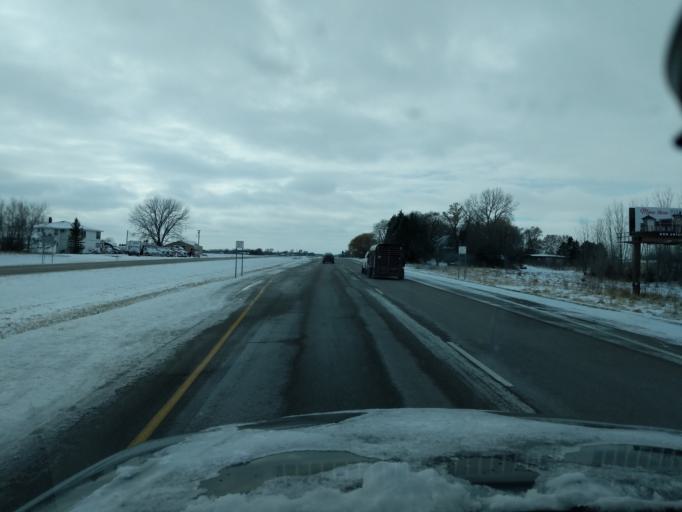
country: US
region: Minnesota
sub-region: Carver County
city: Norwood (historical)
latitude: 44.7683
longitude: -94.0378
